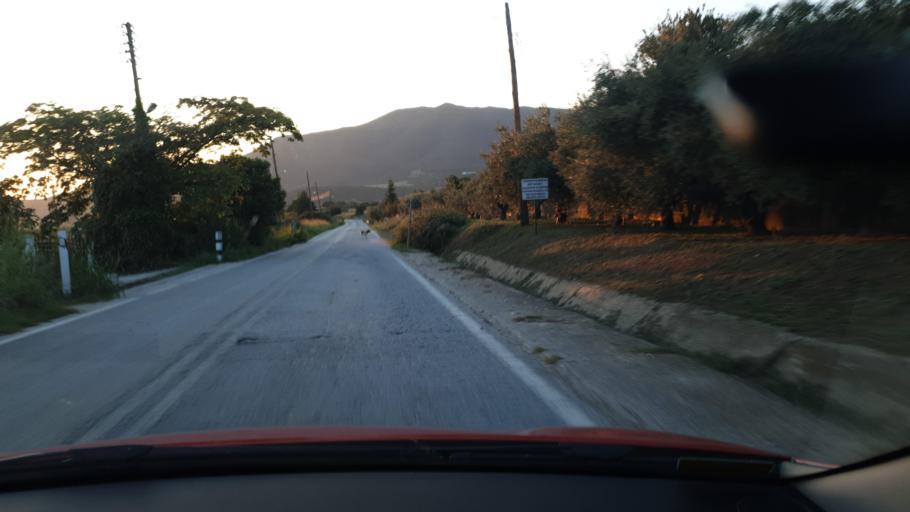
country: GR
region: Central Macedonia
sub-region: Nomos Chalkidikis
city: Galatista
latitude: 40.4683
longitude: 23.2592
